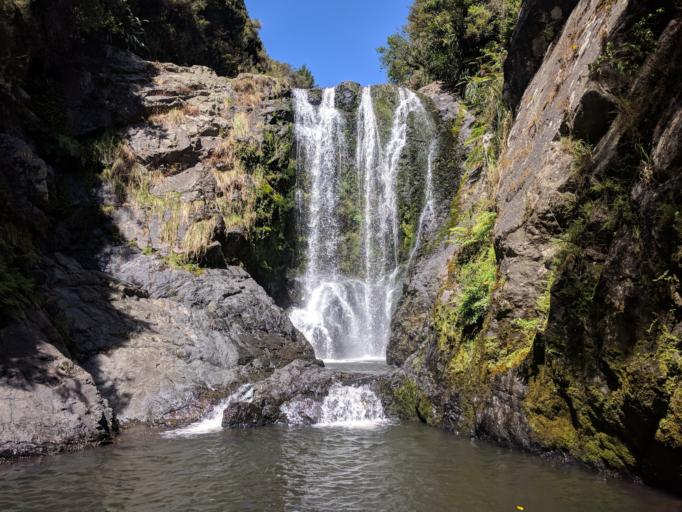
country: NZ
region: Northland
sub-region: Whangarei
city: Ruakaka
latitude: -36.0654
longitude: 174.3896
